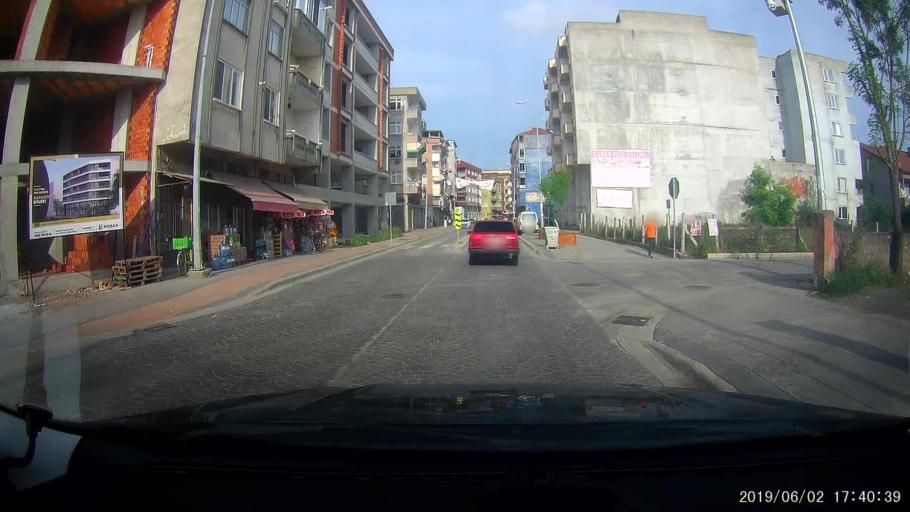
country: TR
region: Samsun
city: Terme
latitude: 41.2109
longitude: 36.9670
